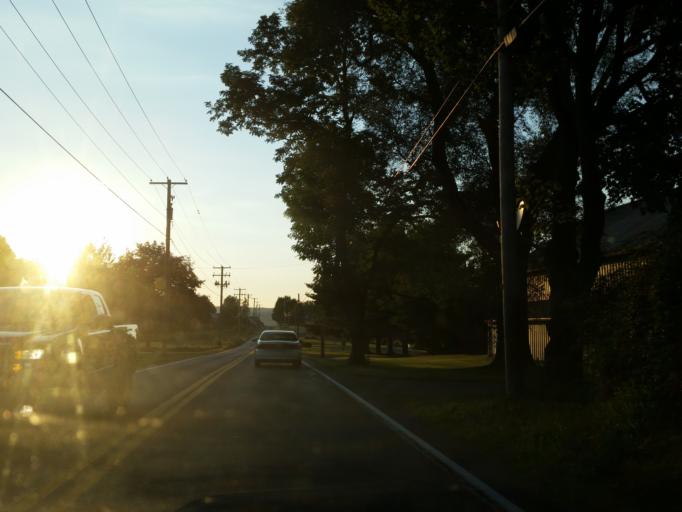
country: US
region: Pennsylvania
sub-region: Lancaster County
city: Reinholds
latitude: 40.2737
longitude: -76.1332
